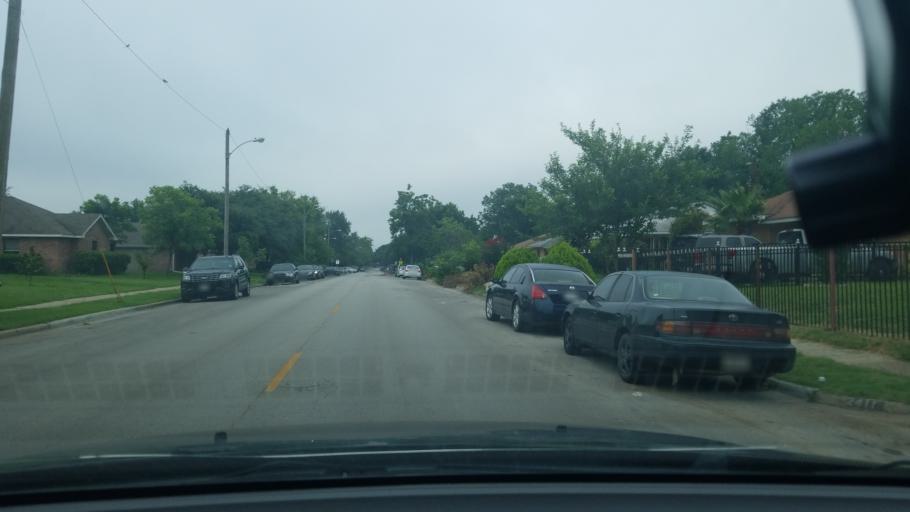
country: US
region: Texas
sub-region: Dallas County
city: Balch Springs
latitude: 32.7542
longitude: -96.6916
